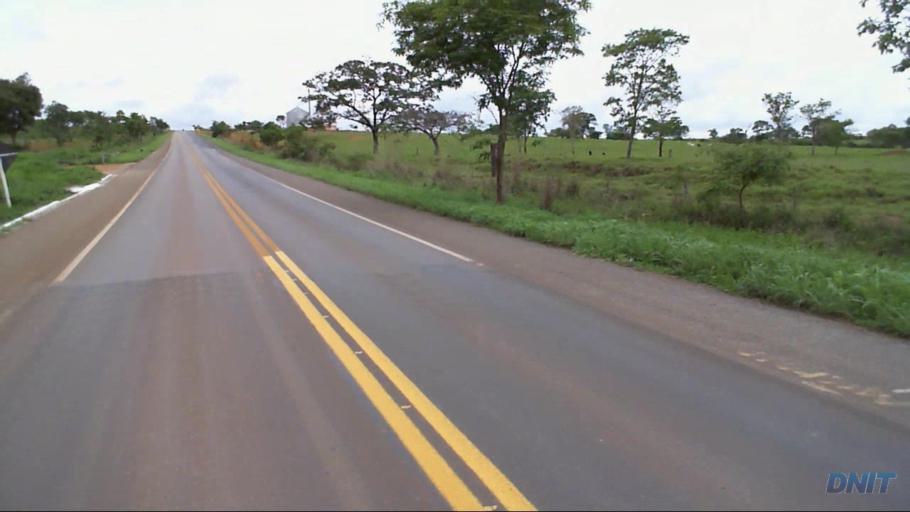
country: BR
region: Goias
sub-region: Padre Bernardo
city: Padre Bernardo
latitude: -15.1568
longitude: -48.3214
